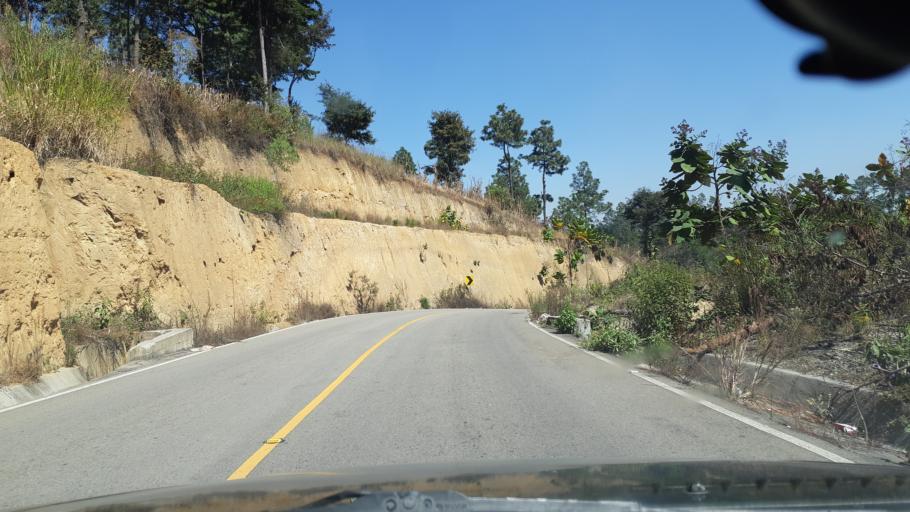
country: GT
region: Chimaltenango
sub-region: Municipio de Zaragoza
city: Zaragoza
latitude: 14.6664
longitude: -90.8587
